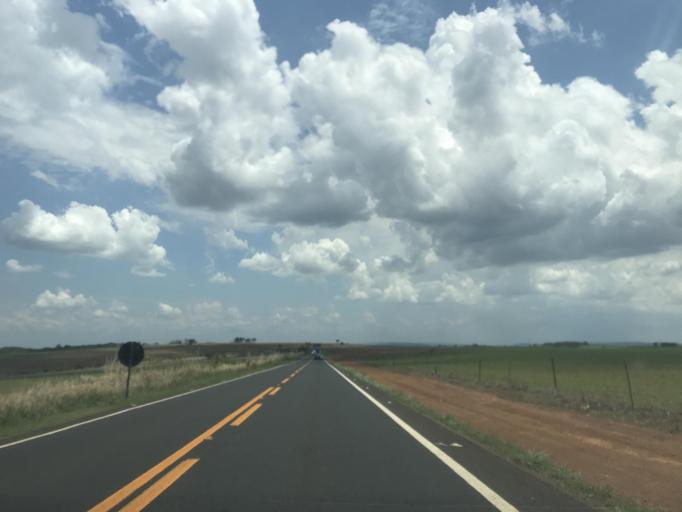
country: BR
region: Goias
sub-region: Piracanjuba
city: Piracanjuba
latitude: -17.4457
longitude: -48.7801
